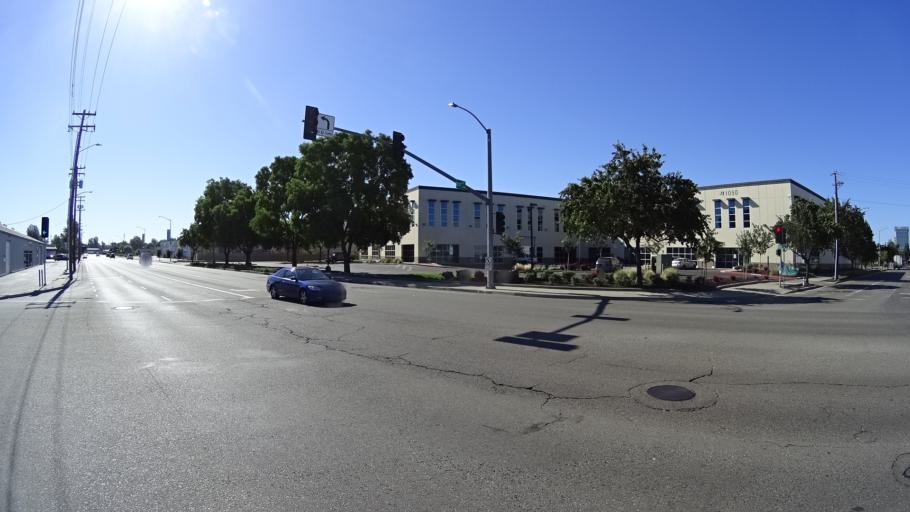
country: US
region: California
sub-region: Sacramento County
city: Sacramento
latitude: 38.5957
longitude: -121.4866
